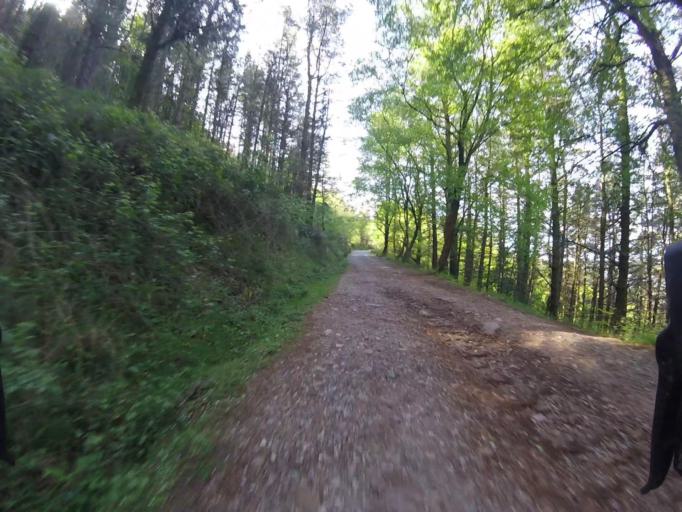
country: ES
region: Basque Country
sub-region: Provincia de Guipuzcoa
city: Andoain
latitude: 43.1991
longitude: -1.9930
